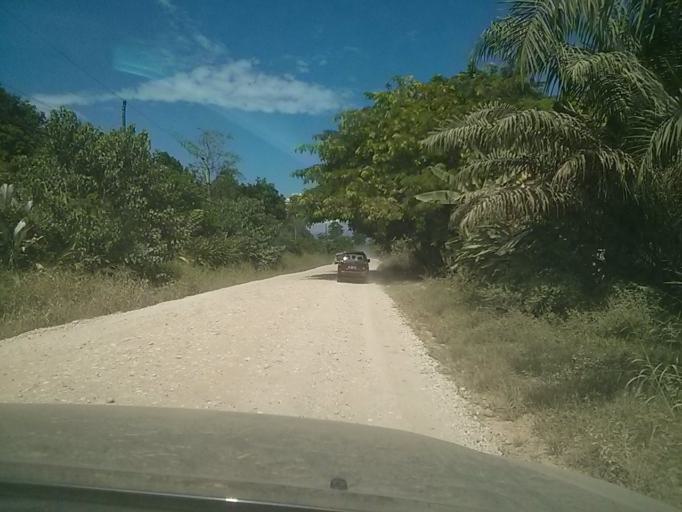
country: CR
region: Puntarenas
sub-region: Canton de Golfito
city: Golfito
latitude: 8.4558
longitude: -83.0493
